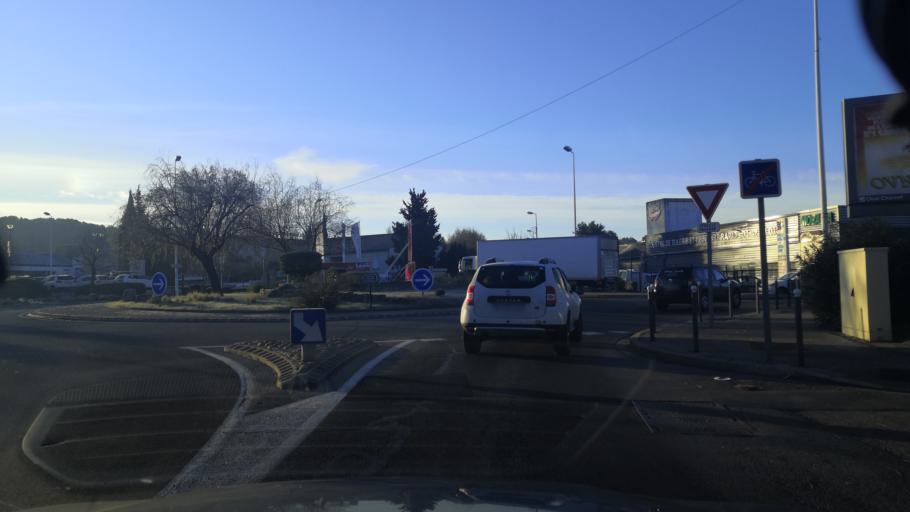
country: FR
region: Provence-Alpes-Cote d'Azur
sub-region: Departement des Bouches-du-Rhone
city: Aix-en-Provence
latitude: 43.5085
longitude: 5.4088
